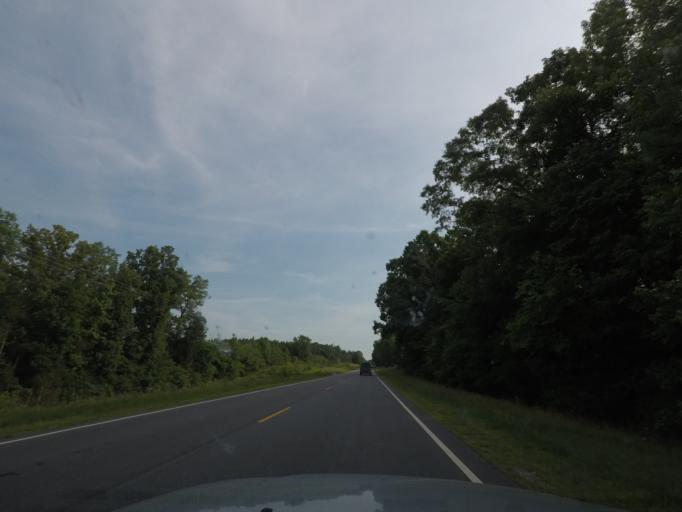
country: US
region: Virginia
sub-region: Mecklenburg County
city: Clarksville
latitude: 36.7643
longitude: -78.6268
